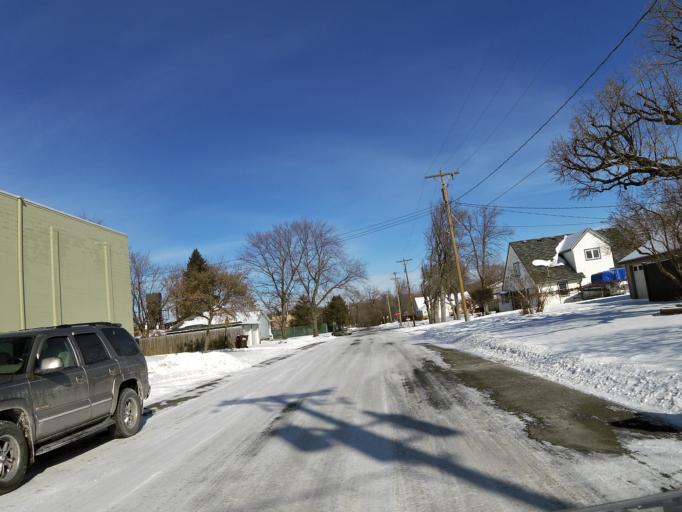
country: US
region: Minnesota
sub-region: Dakota County
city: Hastings
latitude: 44.7435
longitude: -92.8460
